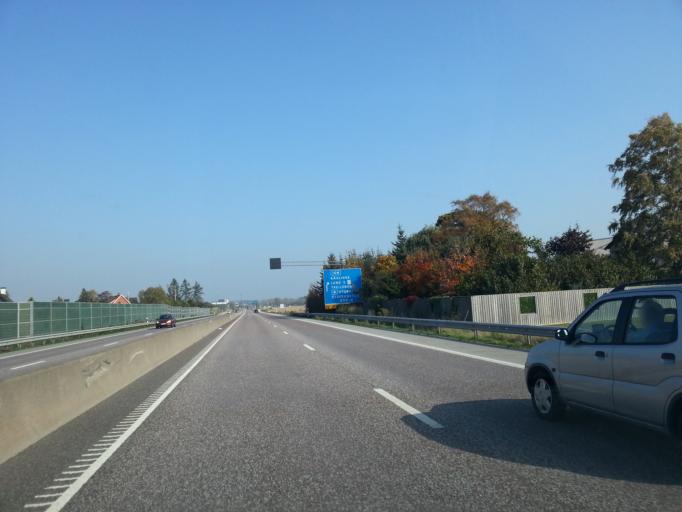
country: SE
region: Skane
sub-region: Staffanstorps Kommun
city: Hjaerup
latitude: 55.6725
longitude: 13.1718
